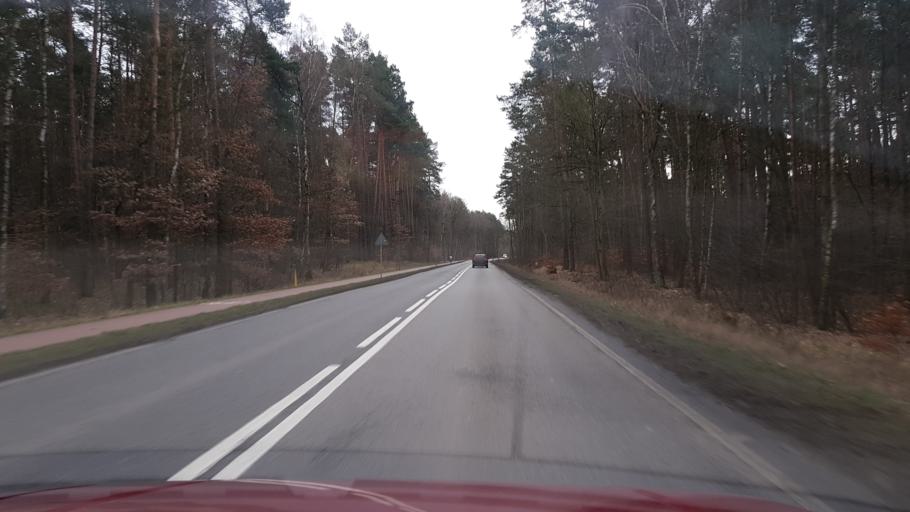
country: PL
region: West Pomeranian Voivodeship
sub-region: Powiat policki
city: Dobra
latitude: 53.5161
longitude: 14.4721
